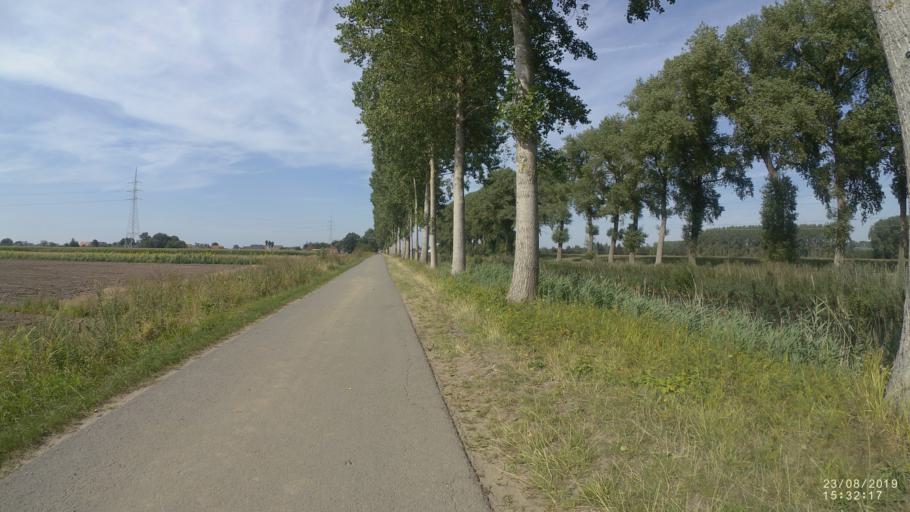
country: BE
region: Flanders
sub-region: Provincie Oost-Vlaanderen
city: Eeklo
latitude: 51.1552
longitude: 3.5491
